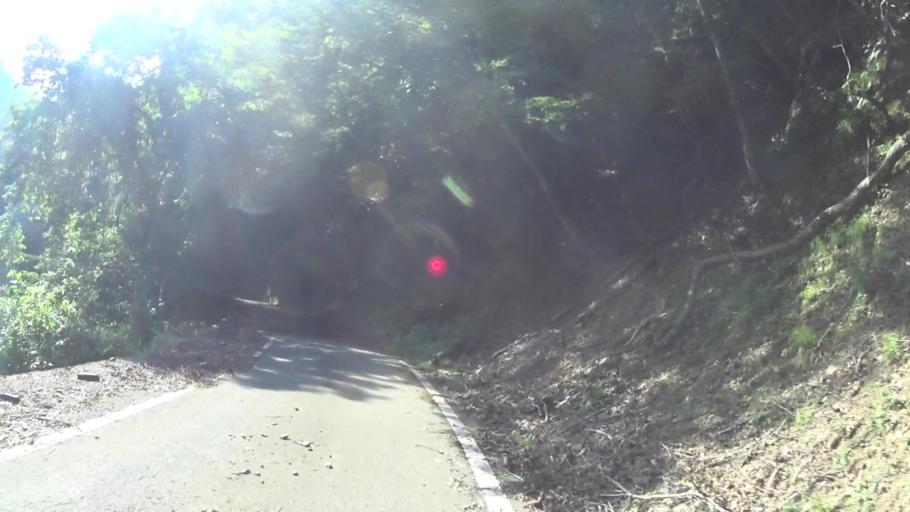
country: JP
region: Fukui
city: Obama
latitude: 35.2720
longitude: 135.6936
